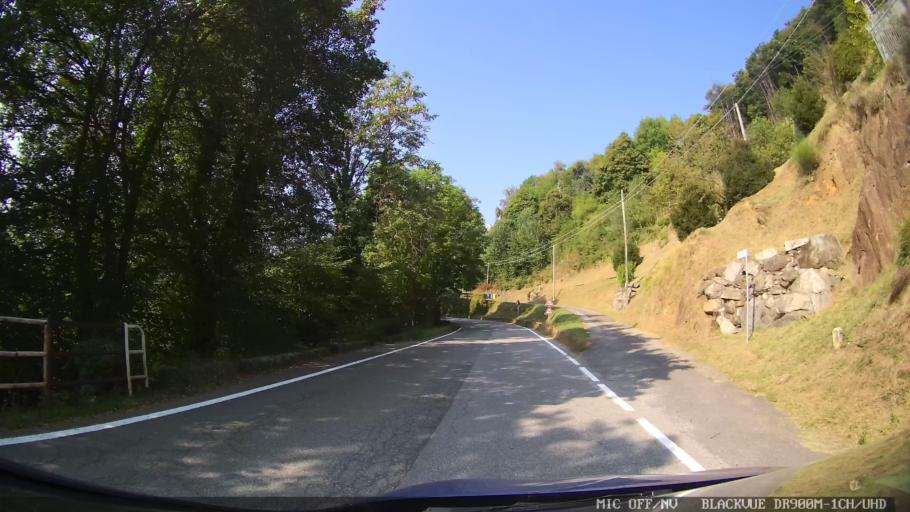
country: IT
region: Piedmont
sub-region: Provincia di Torino
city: Prascorsano
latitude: 45.3644
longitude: 7.6131
